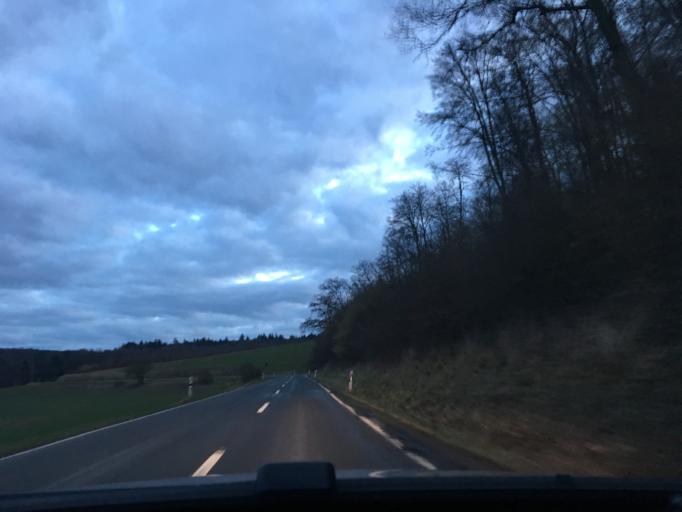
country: DE
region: Rheinland-Pfalz
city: Oberwiesen
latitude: 49.6882
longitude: 7.9657
